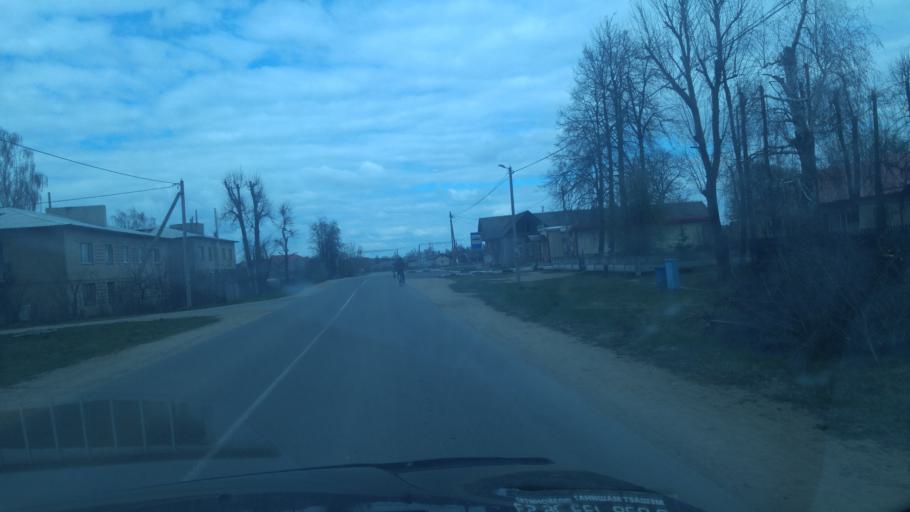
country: BY
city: Michanovichi
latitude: 53.6703
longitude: 27.7487
